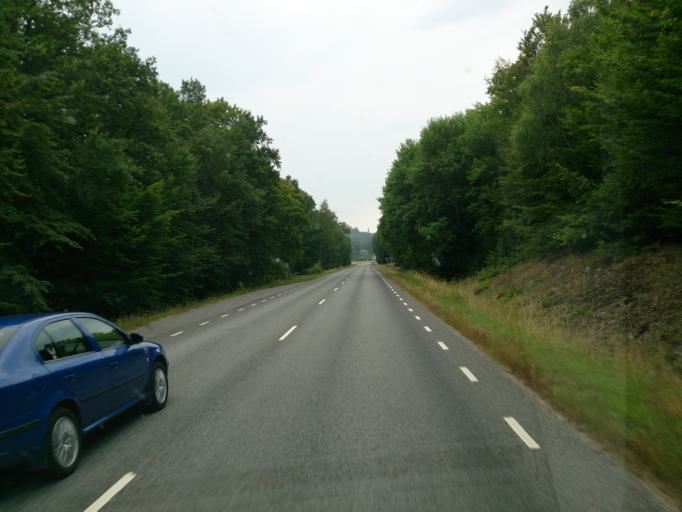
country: SE
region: Skane
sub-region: Kristianstads Kommun
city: Tollarp
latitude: 56.1769
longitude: 14.2834
